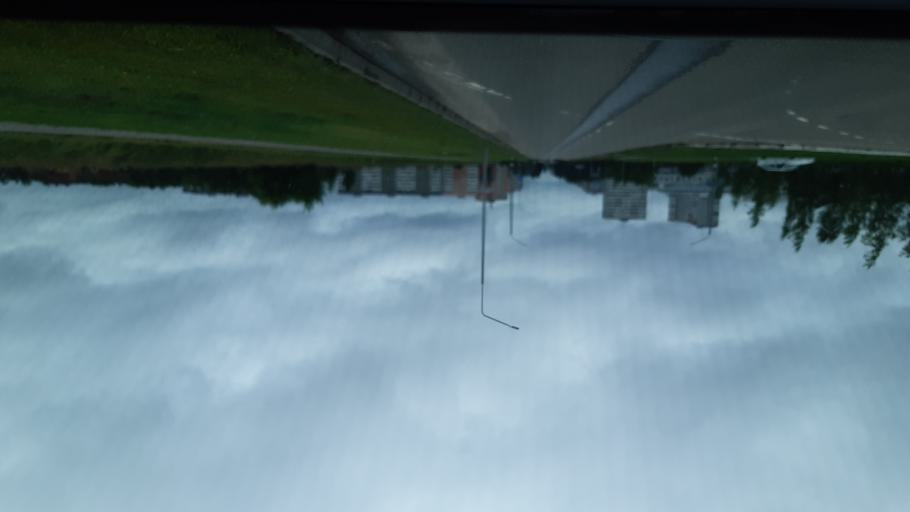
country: RU
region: Smolensk
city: Desnogorsk
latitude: 54.1429
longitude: 33.2800
